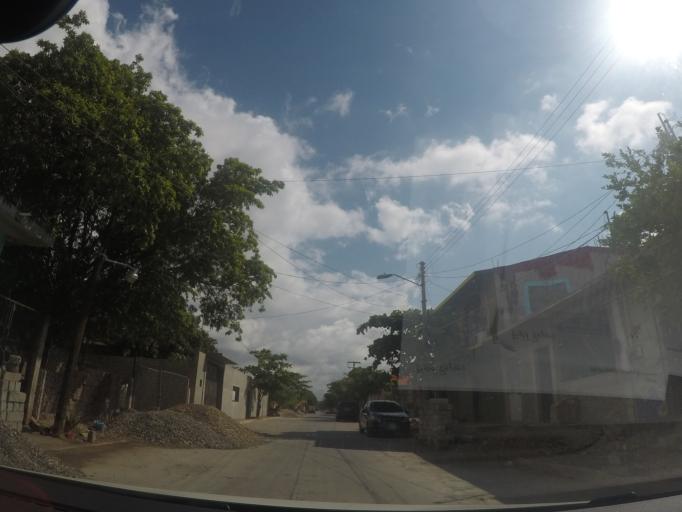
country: MX
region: Oaxaca
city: Juchitan de Zaragoza
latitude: 16.4298
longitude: -95.0284
